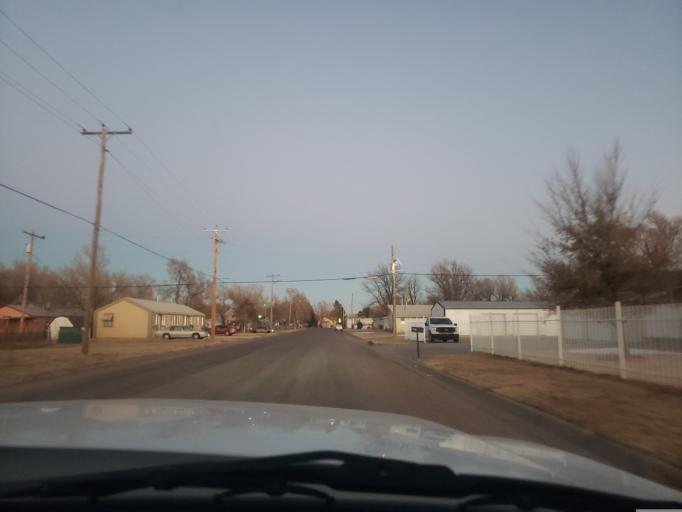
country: US
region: Kansas
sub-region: Finney County
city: Garden City
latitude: 37.9841
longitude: -100.8719
